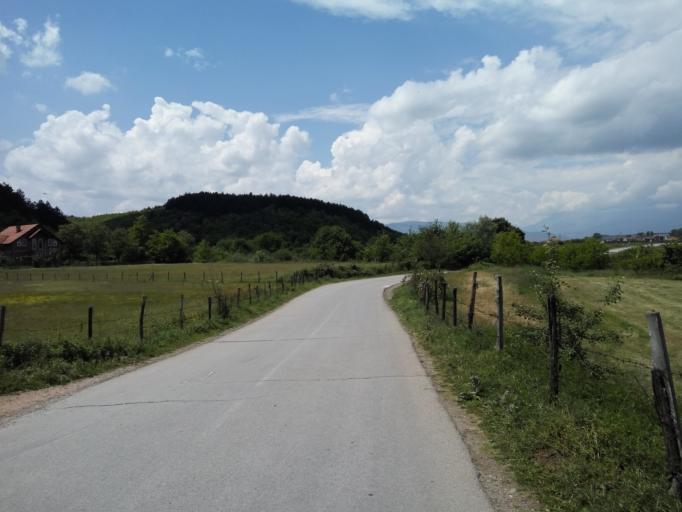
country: XK
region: Gjakova
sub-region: Komuna e Gjakoves
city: Gjakove
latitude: 42.3624
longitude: 20.4314
